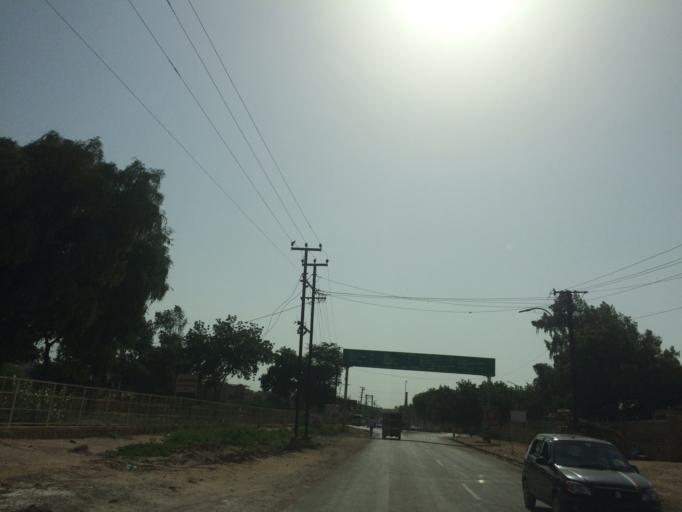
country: IN
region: Rajasthan
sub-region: Jaisalmer
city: Jaisalmer
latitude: 26.9158
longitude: 70.9020
